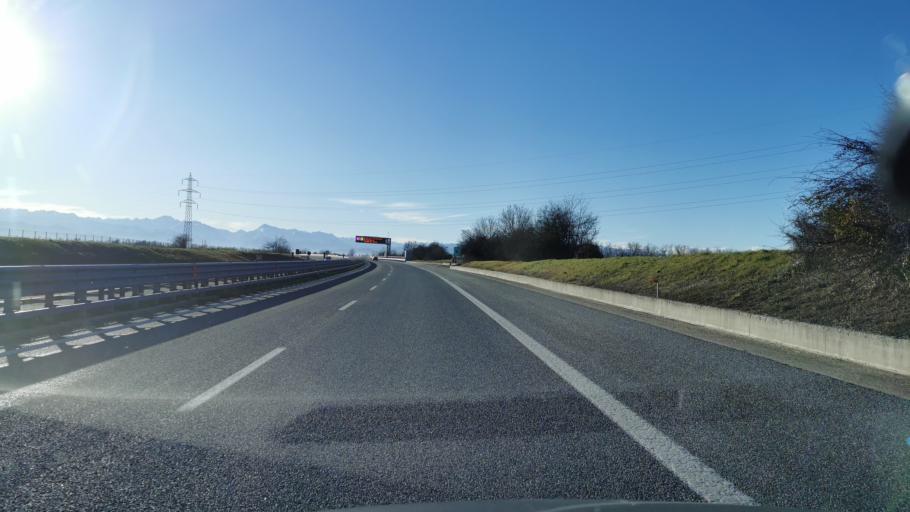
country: IT
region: Piedmont
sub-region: Provincia di Cuneo
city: Magliano Alpi
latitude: 44.4838
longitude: 7.8034
